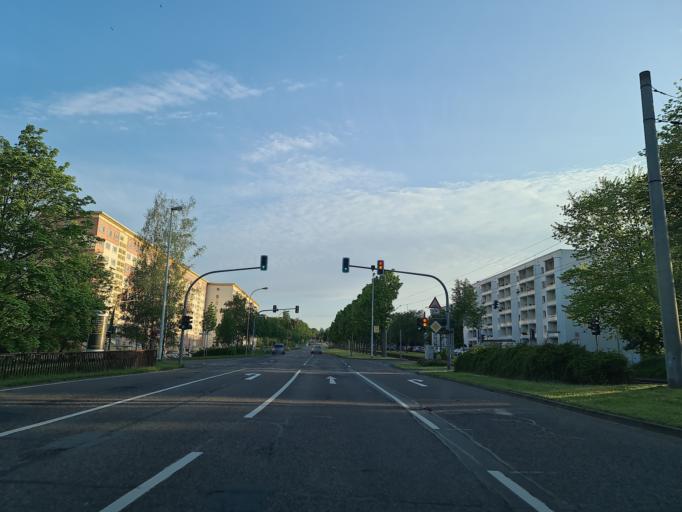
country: DE
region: Saxony
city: Neukirchen
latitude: 50.8079
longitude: 12.8918
